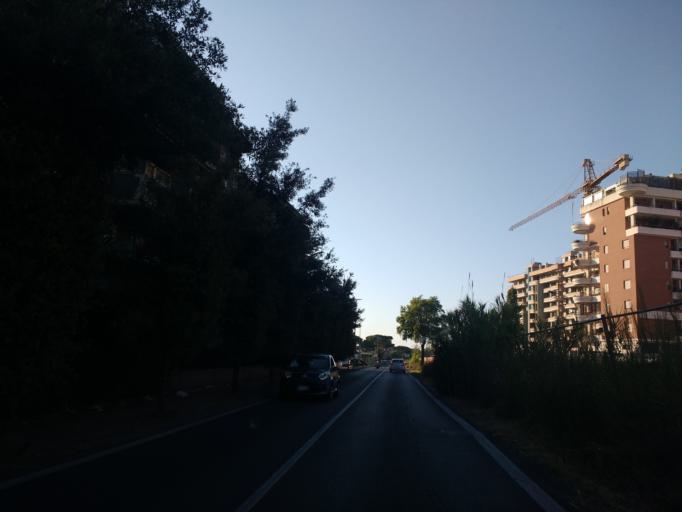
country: IT
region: Latium
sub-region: Citta metropolitana di Roma Capitale
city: Vitinia
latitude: 41.7714
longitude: 12.3730
